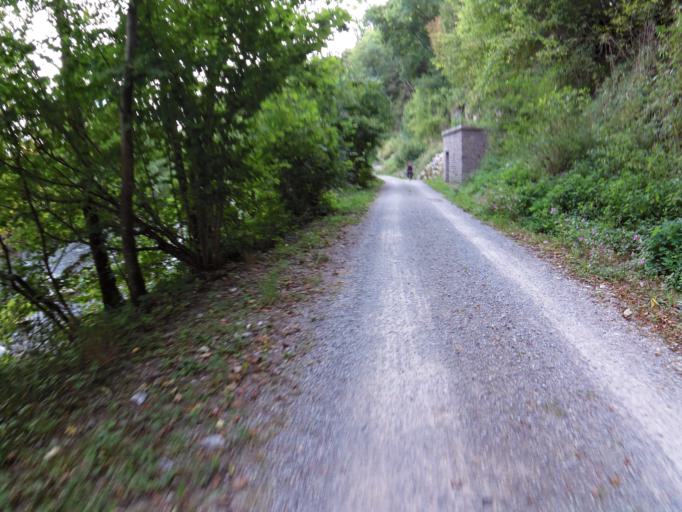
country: DE
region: Baden-Wuerttemberg
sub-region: Freiburg Region
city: Villingendorf
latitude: 48.1992
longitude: 8.6134
